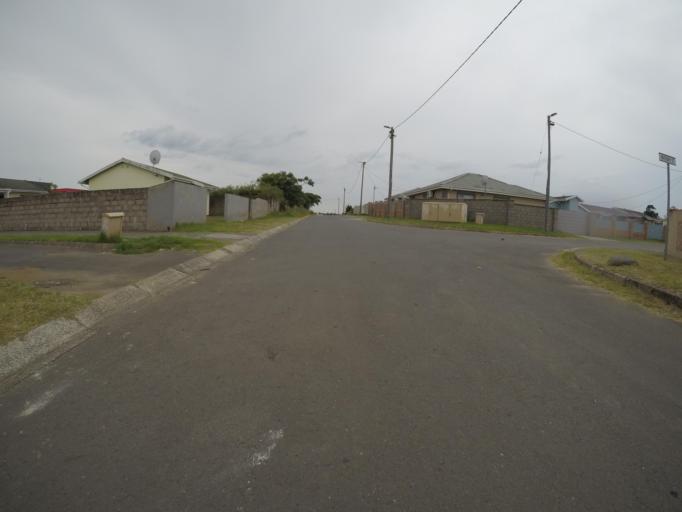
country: ZA
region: Eastern Cape
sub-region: Buffalo City Metropolitan Municipality
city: East London
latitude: -32.9984
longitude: 27.8470
